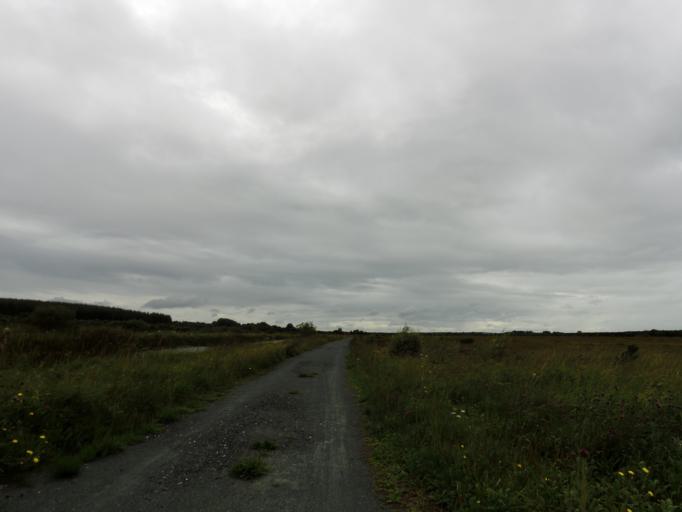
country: IE
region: Leinster
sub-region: An Iarmhi
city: Moate
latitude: 53.5825
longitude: -7.6136
